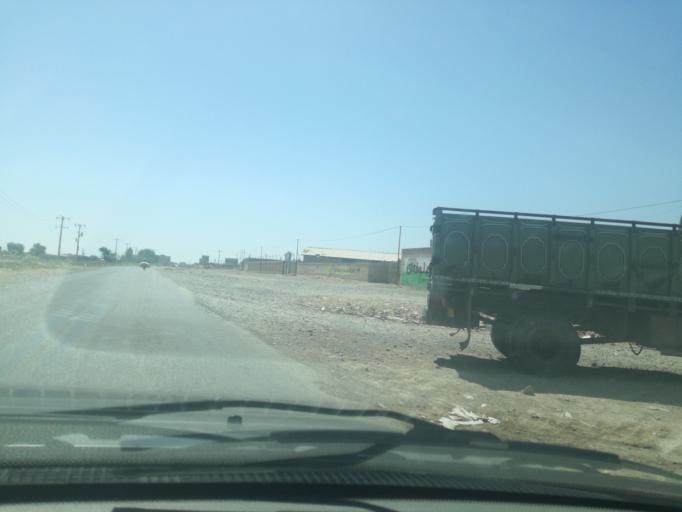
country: IR
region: Razavi Khorasan
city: Sarakhs
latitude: 36.5632
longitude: 61.1459
